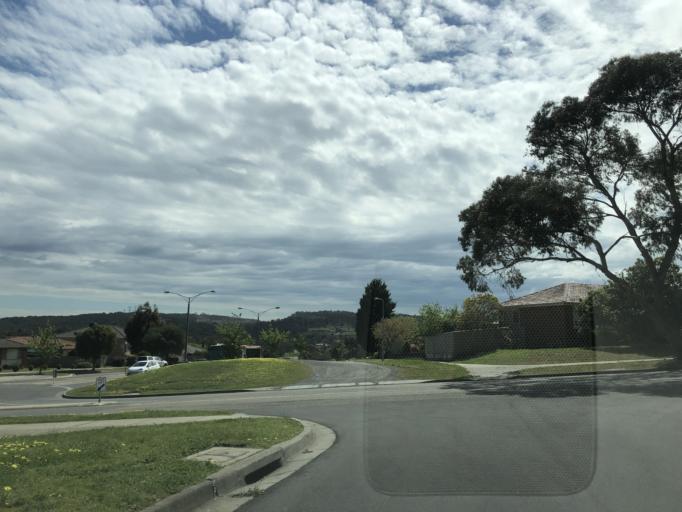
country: AU
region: Victoria
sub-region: Casey
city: Endeavour Hills
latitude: -37.9728
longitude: 145.2608
